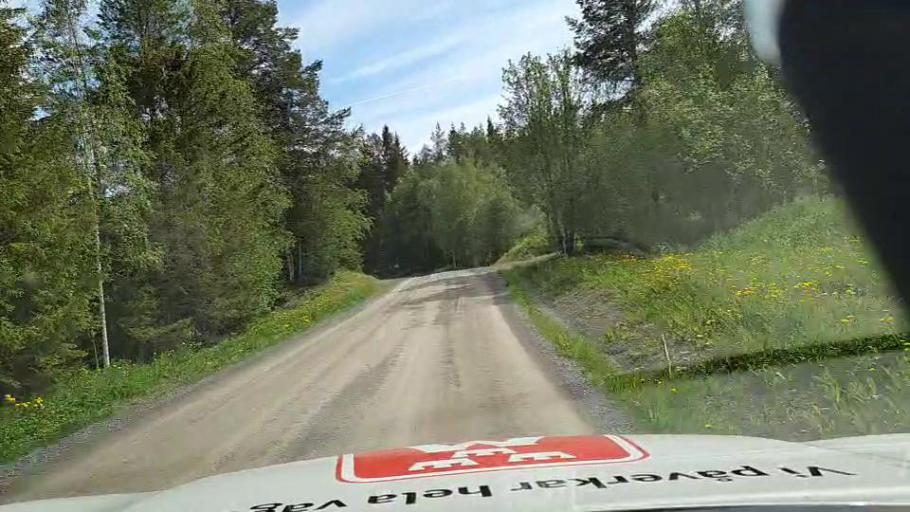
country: SE
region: Jaemtland
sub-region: OEstersunds Kommun
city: Brunflo
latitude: 63.0107
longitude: 14.7827
